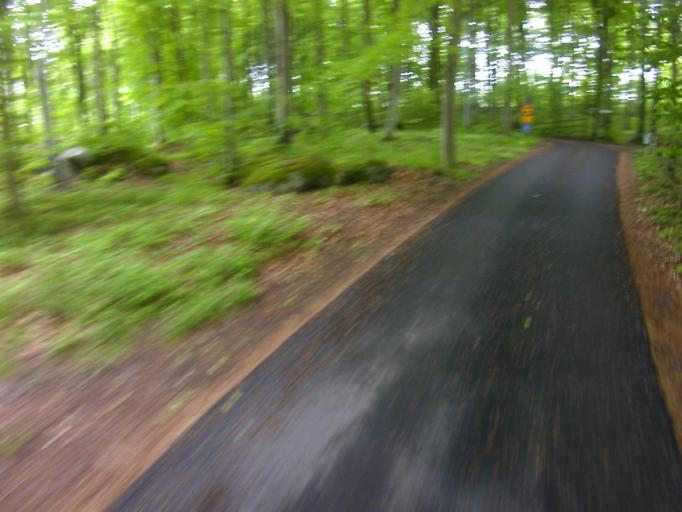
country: SE
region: Blekinge
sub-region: Solvesborgs Kommun
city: Soelvesborg
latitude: 56.0455
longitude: 14.5581
